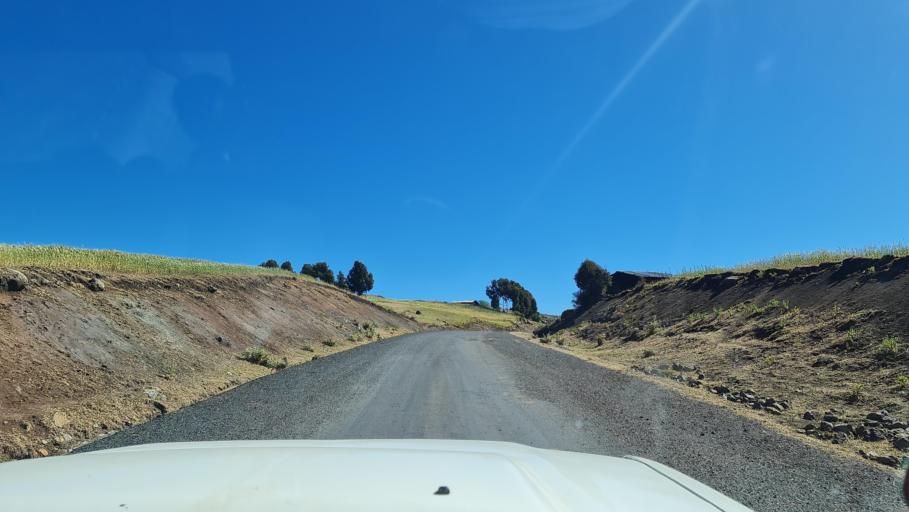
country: ET
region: Amhara
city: Debark'
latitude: 13.1338
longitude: 38.1716
